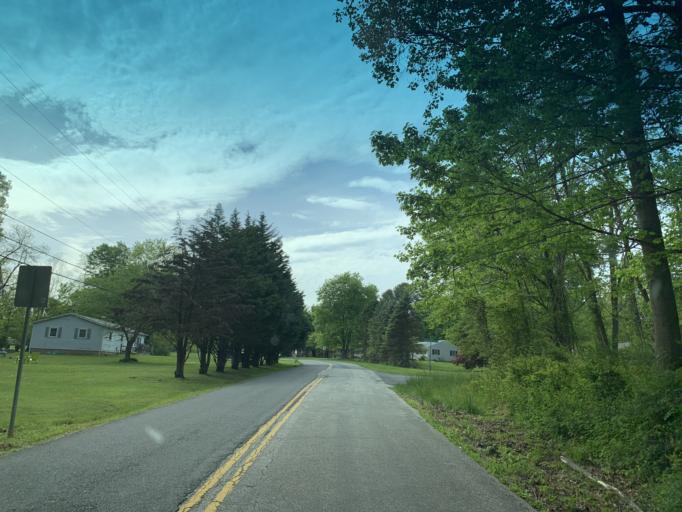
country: US
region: Maryland
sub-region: Harford County
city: South Bel Air
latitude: 39.6437
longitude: -76.2637
